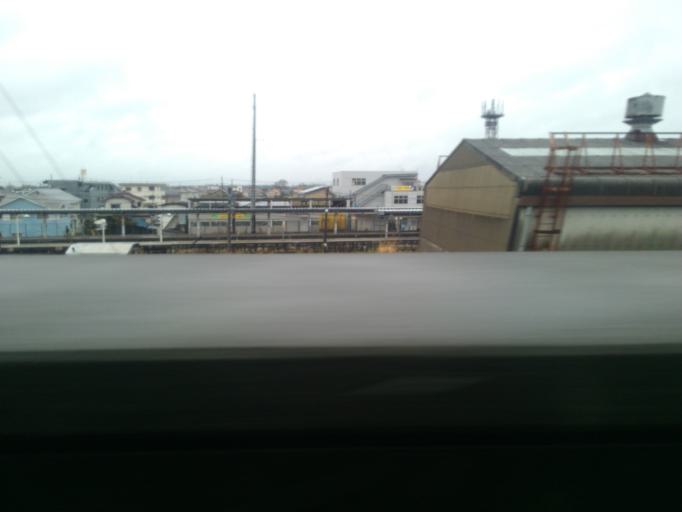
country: JP
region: Tochigi
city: Kaminokawa
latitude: 36.4932
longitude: 139.8777
